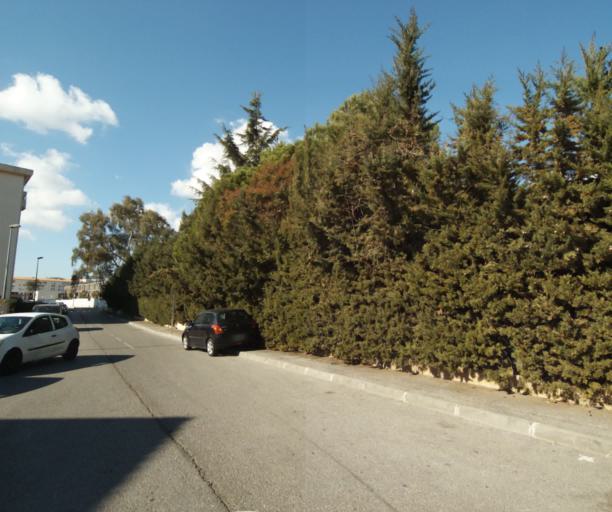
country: FR
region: Provence-Alpes-Cote d'Azur
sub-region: Departement des Alpes-Maritimes
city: Antibes
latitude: 43.5735
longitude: 7.0957
